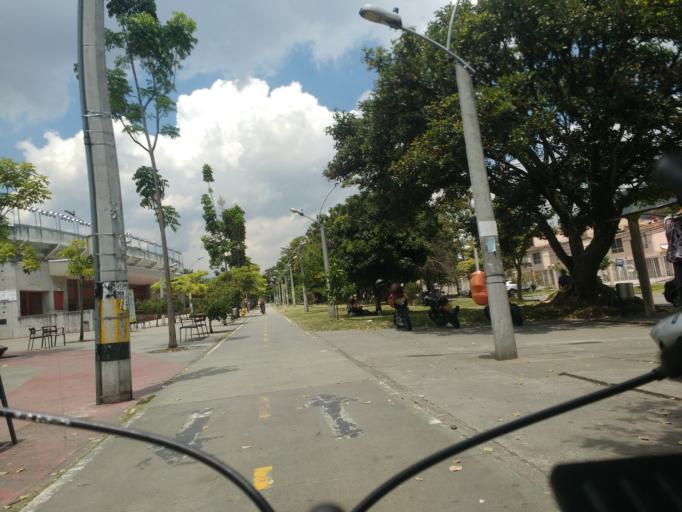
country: CO
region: Antioquia
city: Itagui
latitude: 6.2158
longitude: -75.5932
